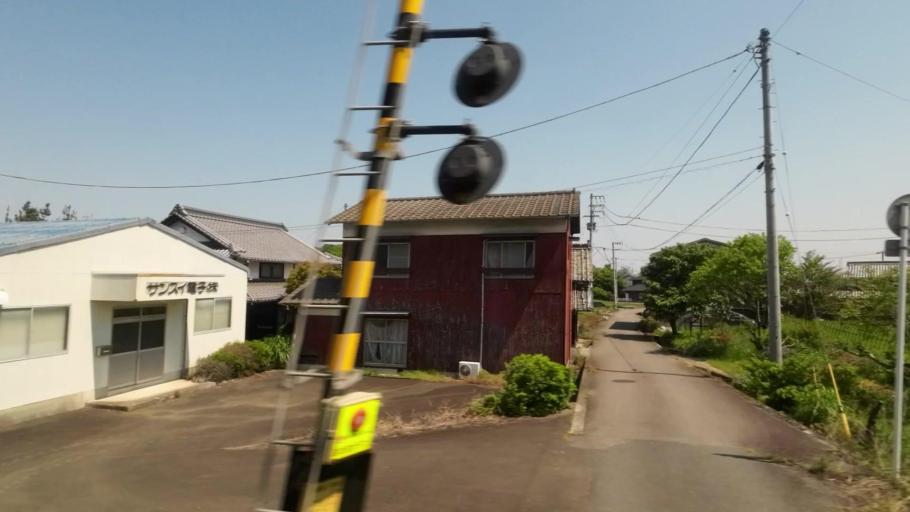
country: JP
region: Ehime
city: Saijo
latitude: 33.8969
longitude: 133.1285
